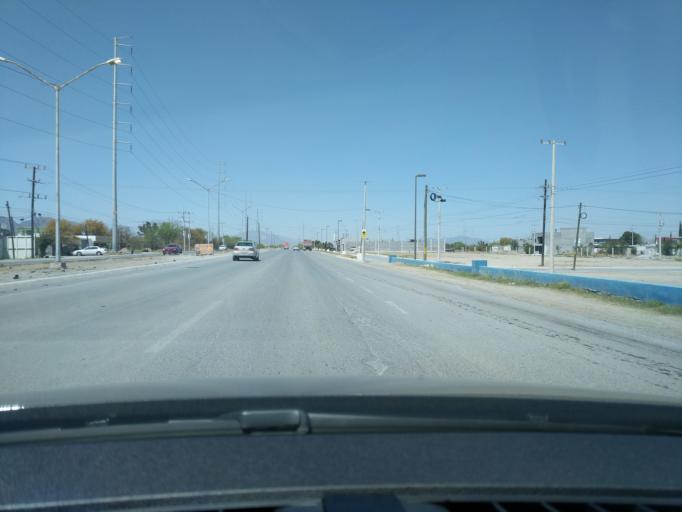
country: MX
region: Nuevo Leon
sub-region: Salinas Victoria
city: Emiliano Zapata
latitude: 25.9152
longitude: -100.2686
